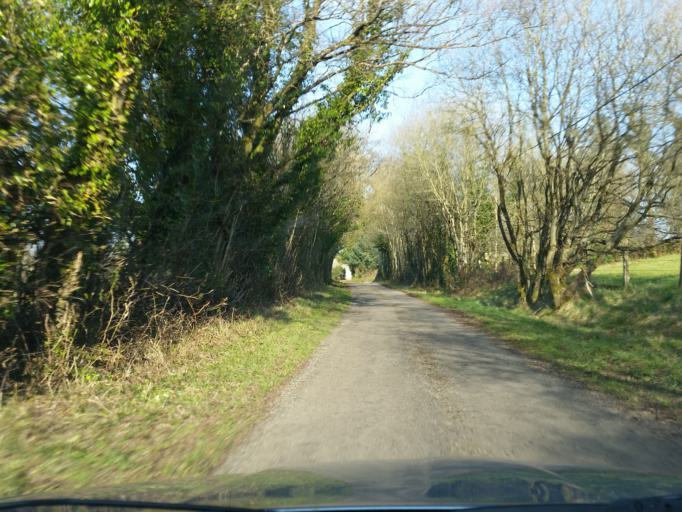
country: IE
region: Ulster
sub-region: County Monaghan
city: Clones
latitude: 54.2282
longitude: -7.2313
